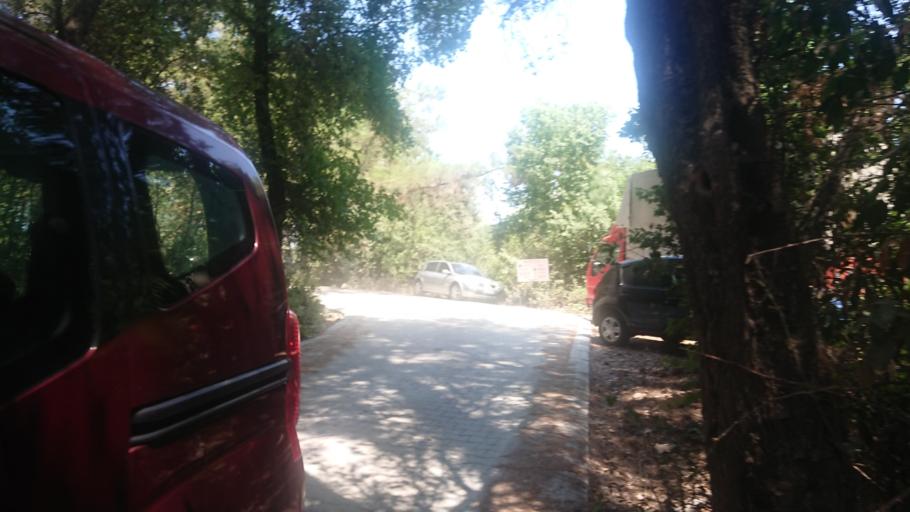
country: TR
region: Aydin
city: Atburgazi
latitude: 37.6985
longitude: 27.1733
